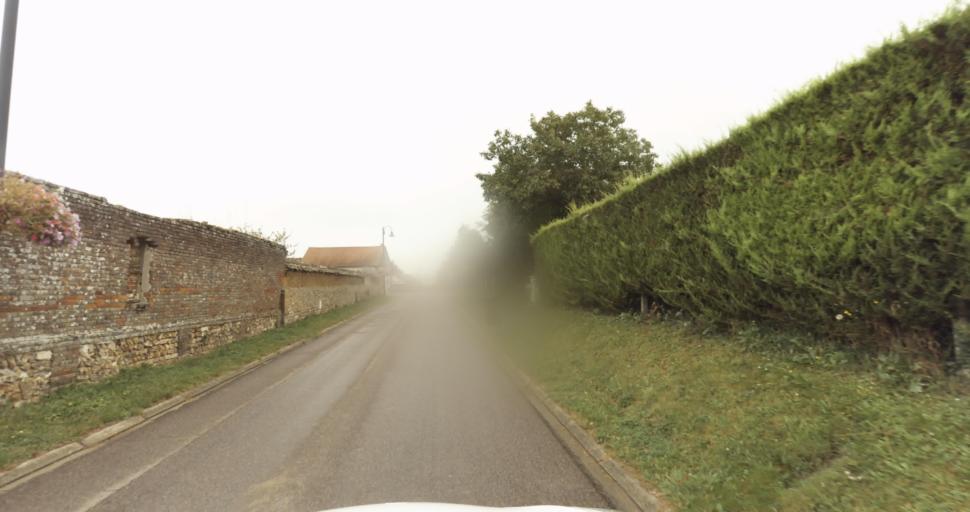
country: FR
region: Haute-Normandie
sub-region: Departement de l'Eure
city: Gravigny
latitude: 49.0824
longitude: 1.2085
